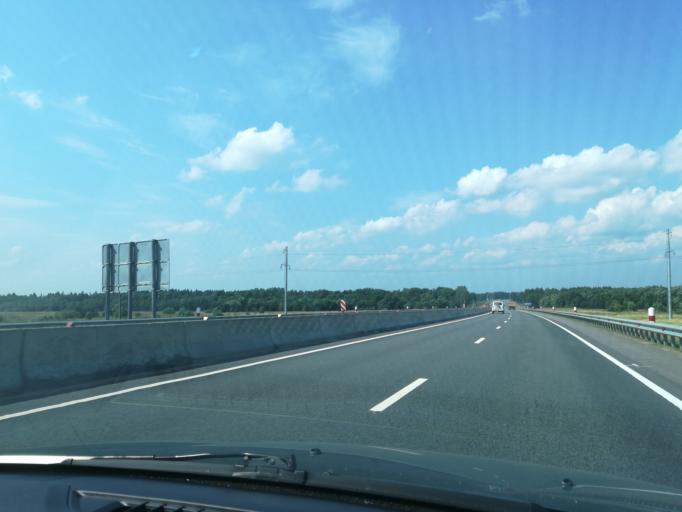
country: RU
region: Leningrad
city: Kingisepp
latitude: 59.5951
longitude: 28.7377
